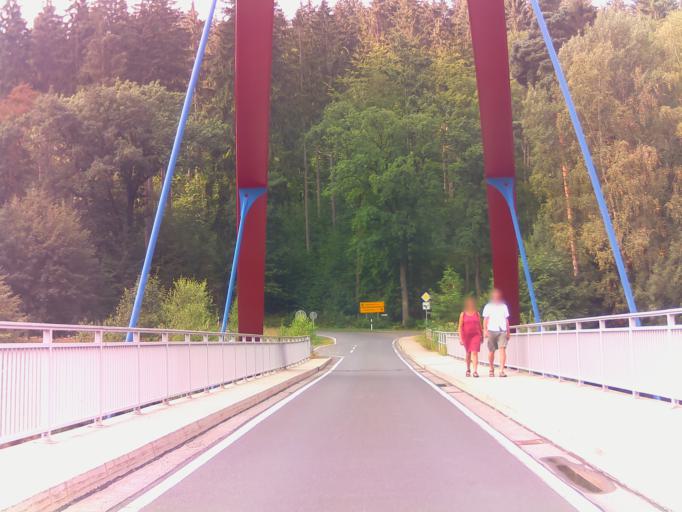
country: DE
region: Thuringia
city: Burgk
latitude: 50.5476
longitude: 11.7259
